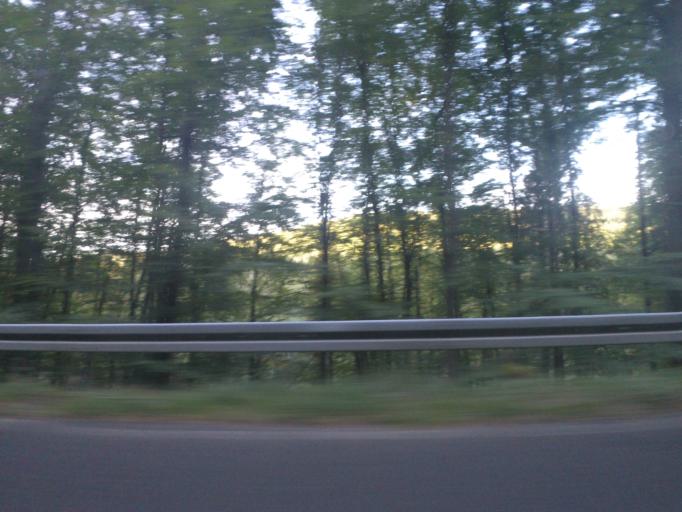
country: DE
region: Hesse
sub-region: Regierungsbezirk Darmstadt
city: Gelnhausen
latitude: 50.2681
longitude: 9.2158
